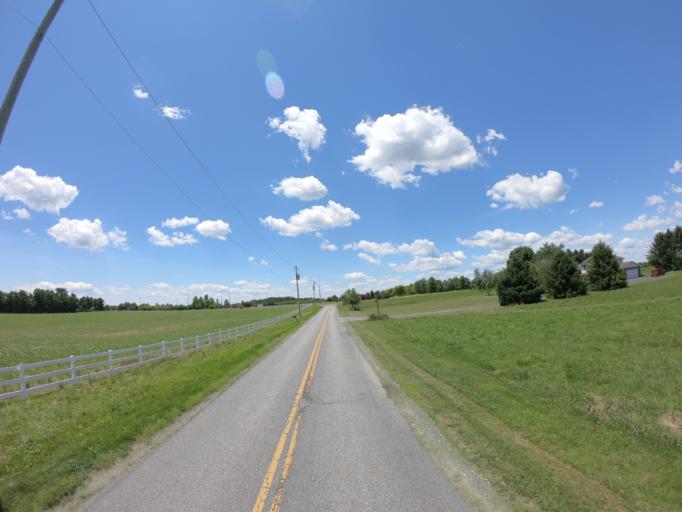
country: US
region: Delaware
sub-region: New Castle County
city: Middletown
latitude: 39.4809
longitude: -75.7756
